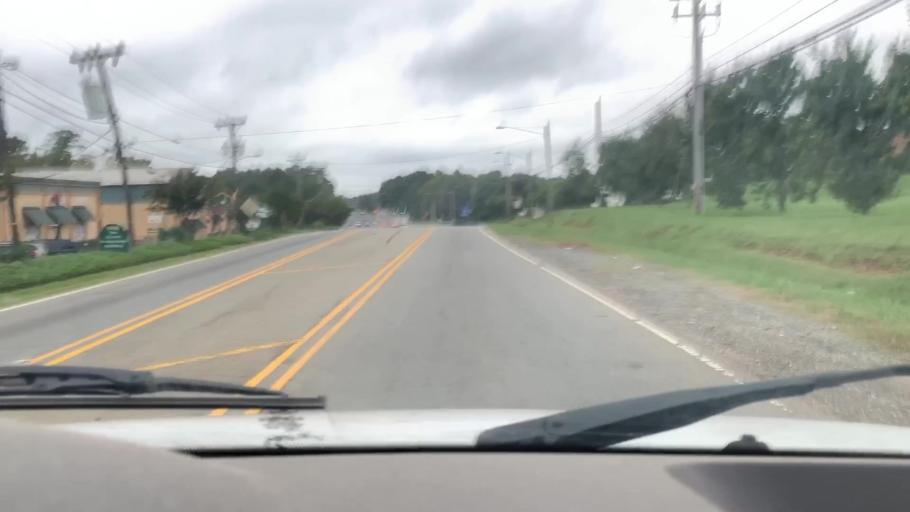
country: US
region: North Carolina
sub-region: Mecklenburg County
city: Huntersville
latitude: 35.3383
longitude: -80.8244
